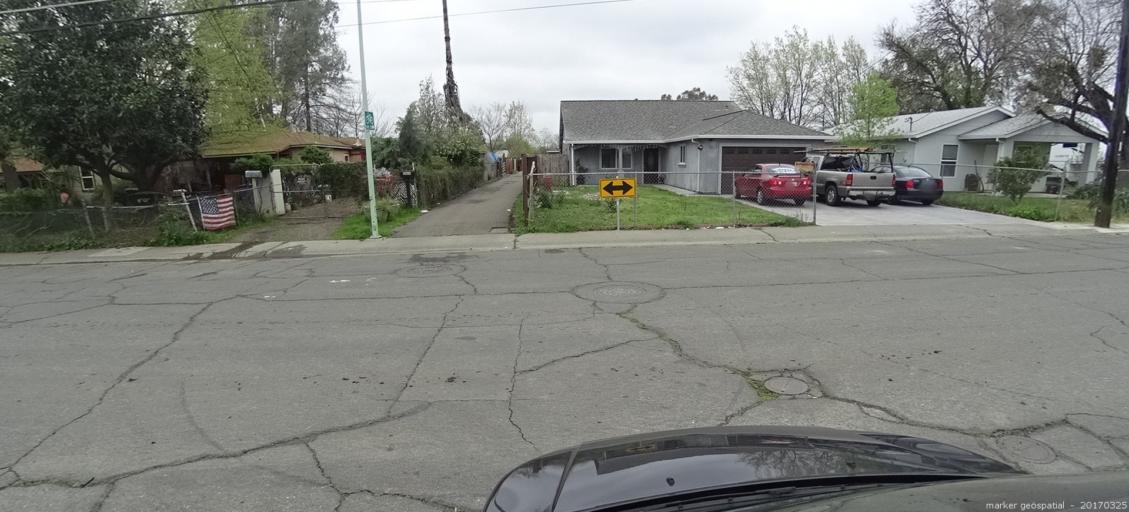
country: US
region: California
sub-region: Sacramento County
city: Florin
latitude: 38.5205
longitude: -121.4144
